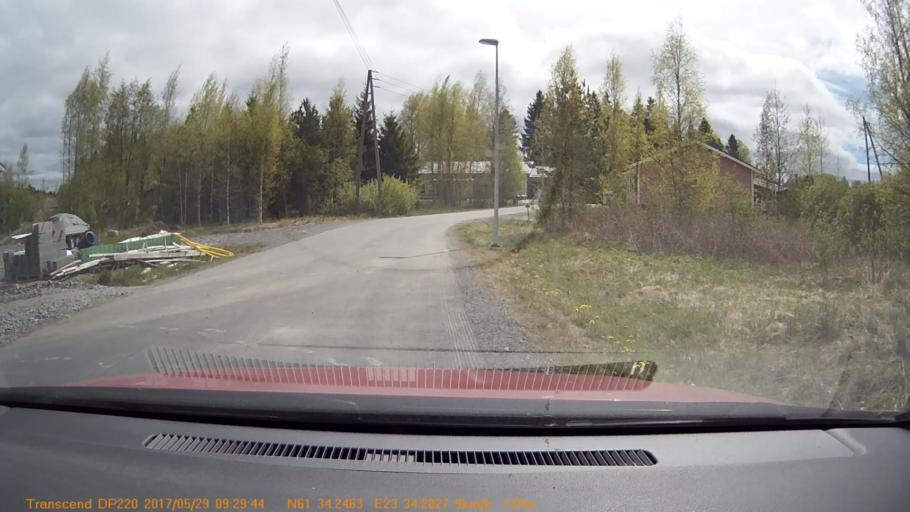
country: FI
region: Pirkanmaa
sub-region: Tampere
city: Yloejaervi
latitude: 61.5708
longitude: 23.5714
